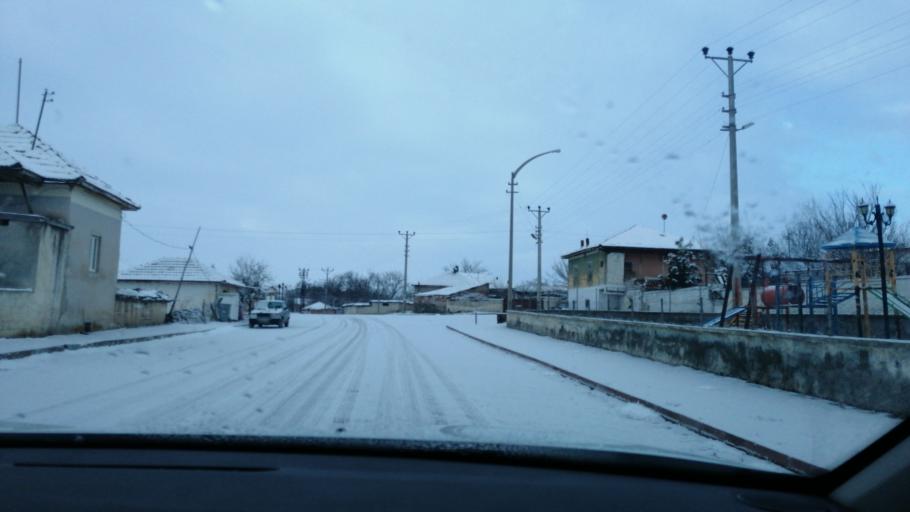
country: TR
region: Aksaray
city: Agacoren
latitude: 38.9330
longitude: 33.9489
